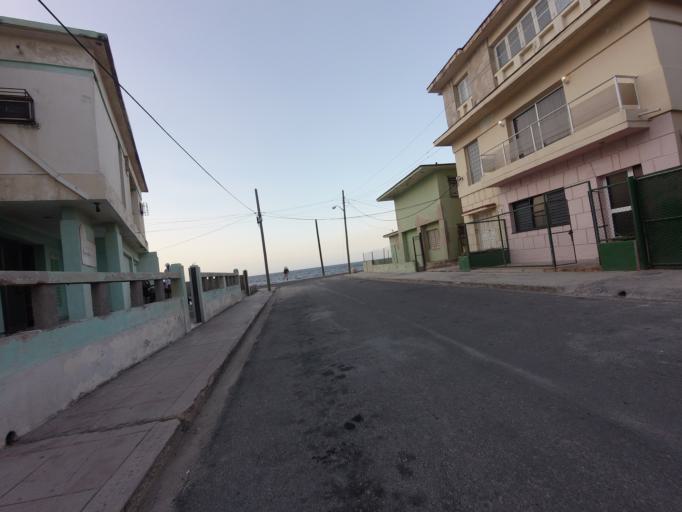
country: CU
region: La Habana
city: Cerro
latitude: 23.0954
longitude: -82.4612
